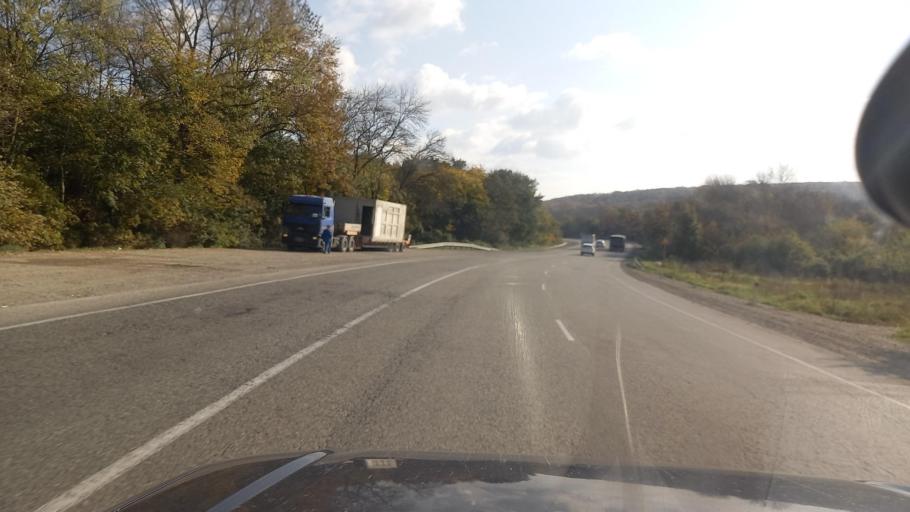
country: RU
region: Krasnodarskiy
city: Gayduk
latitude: 44.8741
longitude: 37.7662
